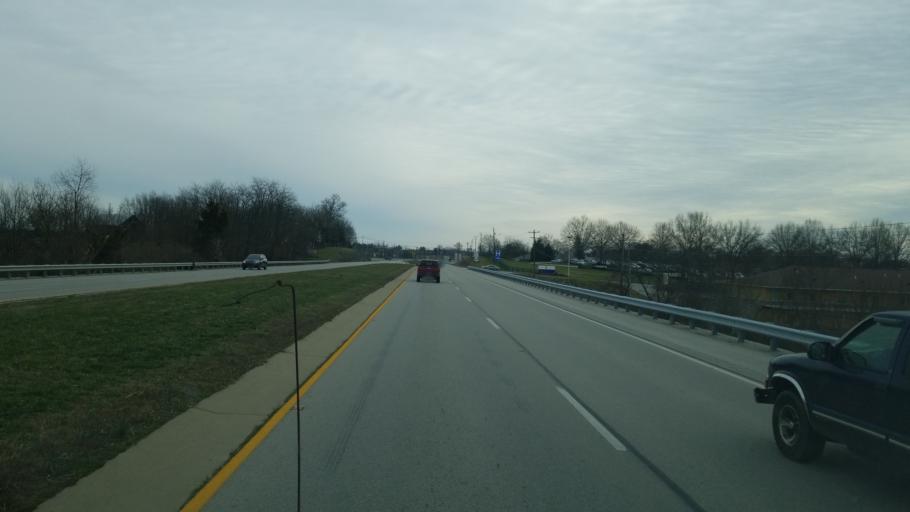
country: US
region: Kentucky
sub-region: Bourbon County
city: Paris
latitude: 38.2236
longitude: -84.2399
